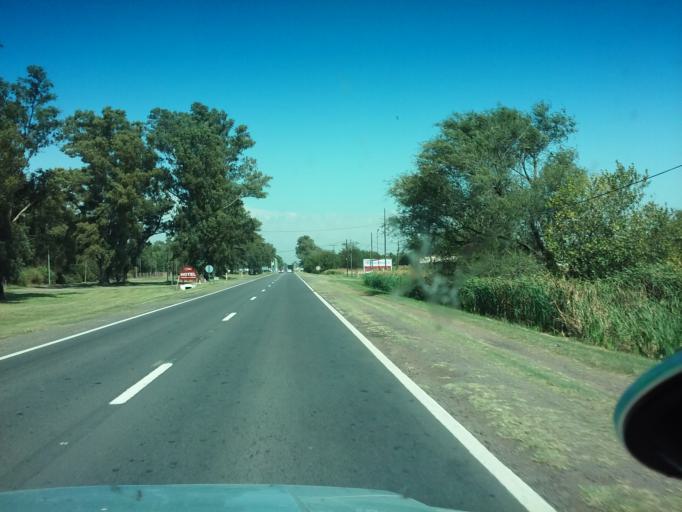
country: AR
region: Buenos Aires
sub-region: Partido de Nueve de Julio
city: Nueve de Julio
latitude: -35.4858
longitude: -60.8839
